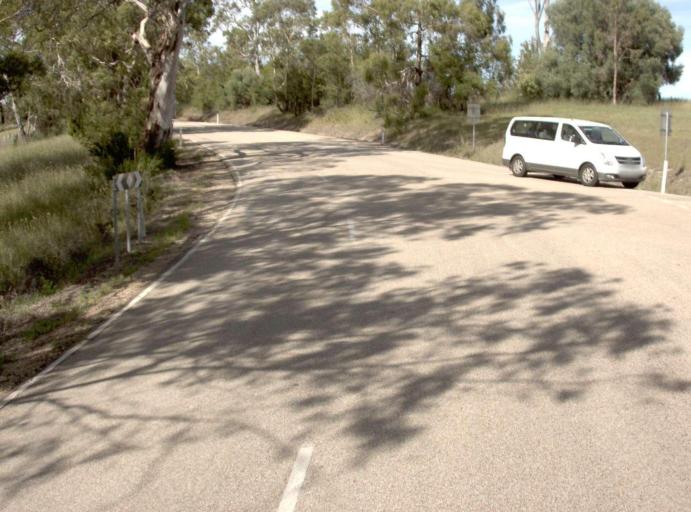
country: AU
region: Victoria
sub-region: East Gippsland
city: Lakes Entrance
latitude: -37.5162
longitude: 148.1636
